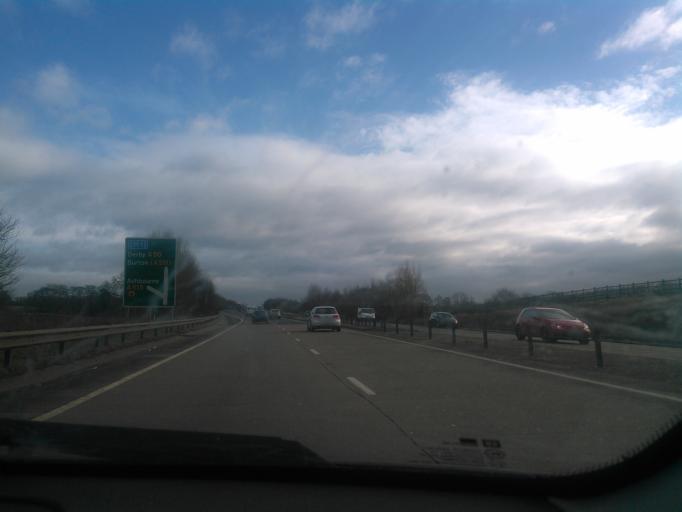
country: GB
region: England
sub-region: Staffordshire
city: Uttoxeter
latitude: 52.8956
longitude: -1.7833
